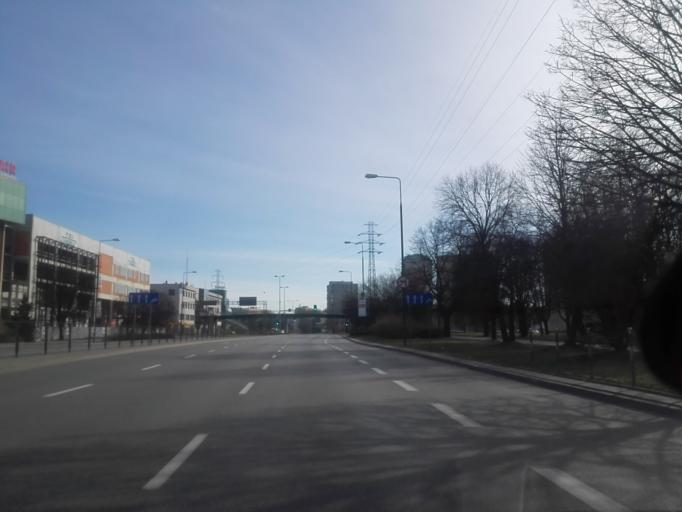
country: PL
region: Masovian Voivodeship
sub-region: Warszawa
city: Mokotow
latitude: 52.1765
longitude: 21.0022
